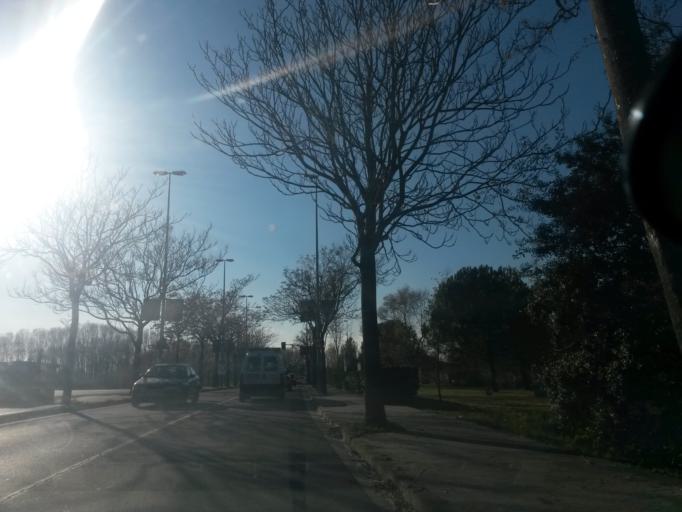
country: ES
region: Catalonia
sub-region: Provincia de Girona
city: Girona
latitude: 41.9914
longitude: 2.8105
